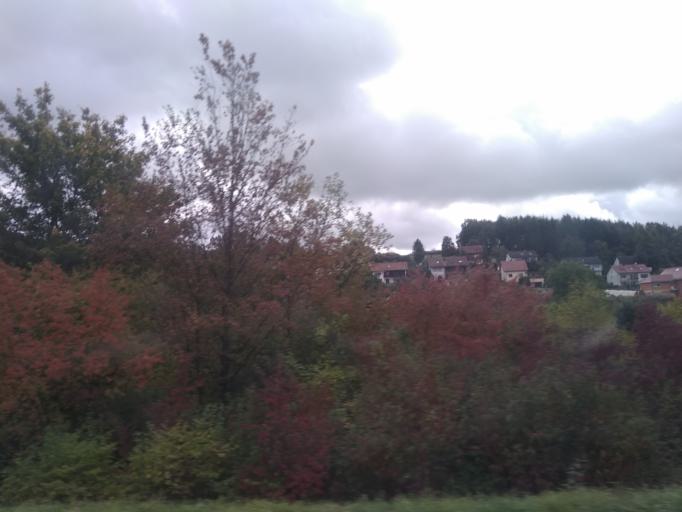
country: DE
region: Baden-Wuerttemberg
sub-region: Karlsruhe Region
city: Billigheim
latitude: 49.3764
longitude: 9.2687
